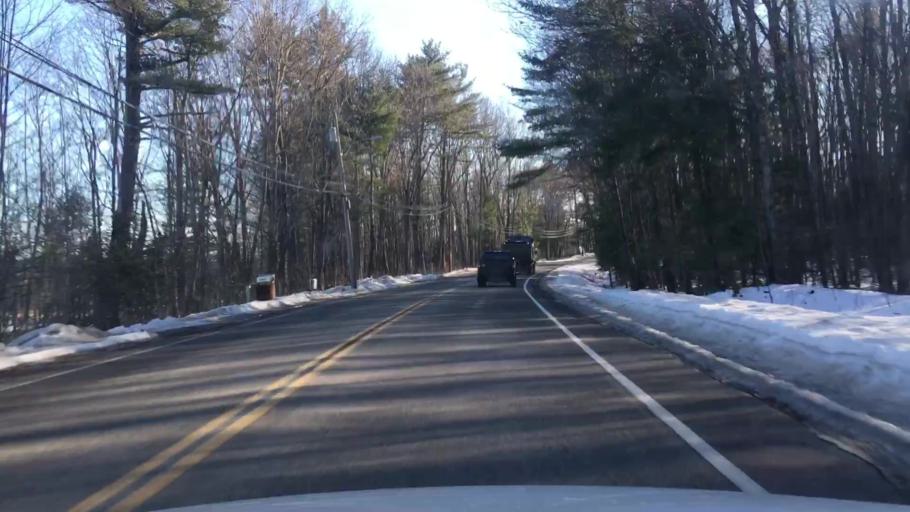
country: US
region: Maine
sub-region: Cumberland County
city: Westbrook
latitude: 43.6993
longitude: -70.3569
